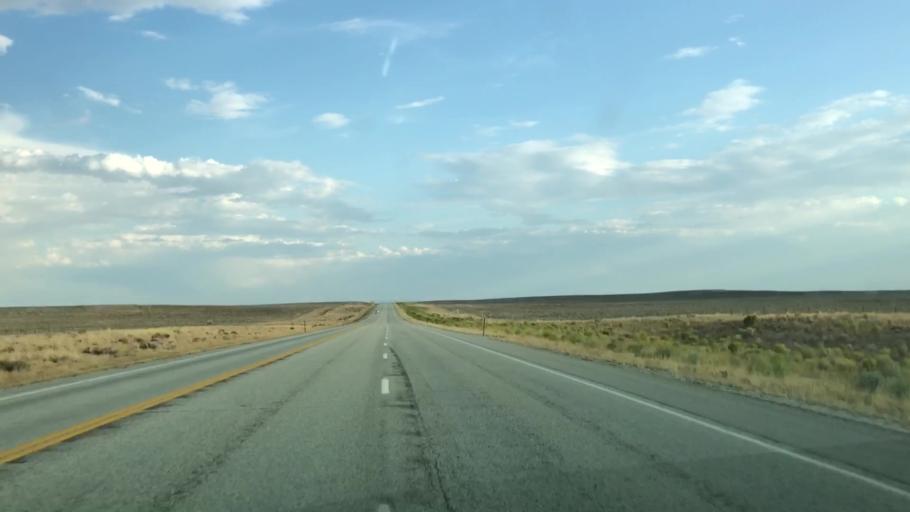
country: US
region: Wyoming
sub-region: Sweetwater County
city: North Rock Springs
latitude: 42.2722
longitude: -109.4800
